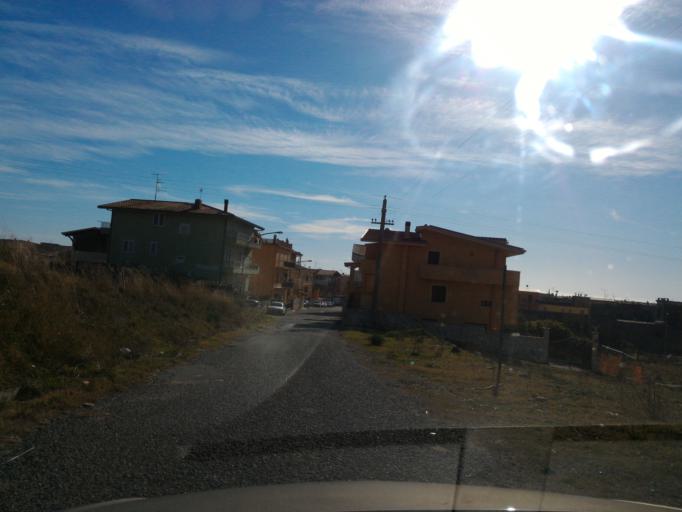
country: IT
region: Calabria
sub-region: Provincia di Catanzaro
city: Cropani Marina
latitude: 38.9256
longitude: 16.8093
